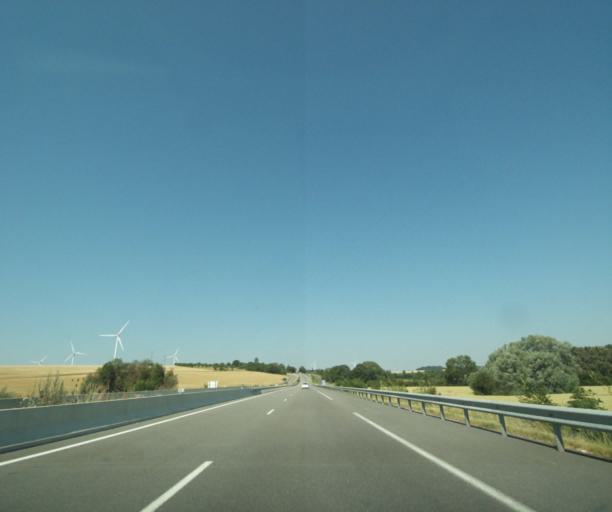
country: FR
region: Lorraine
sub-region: Departement de la Meuse
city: Lerouville
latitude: 48.7046
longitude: 5.4565
